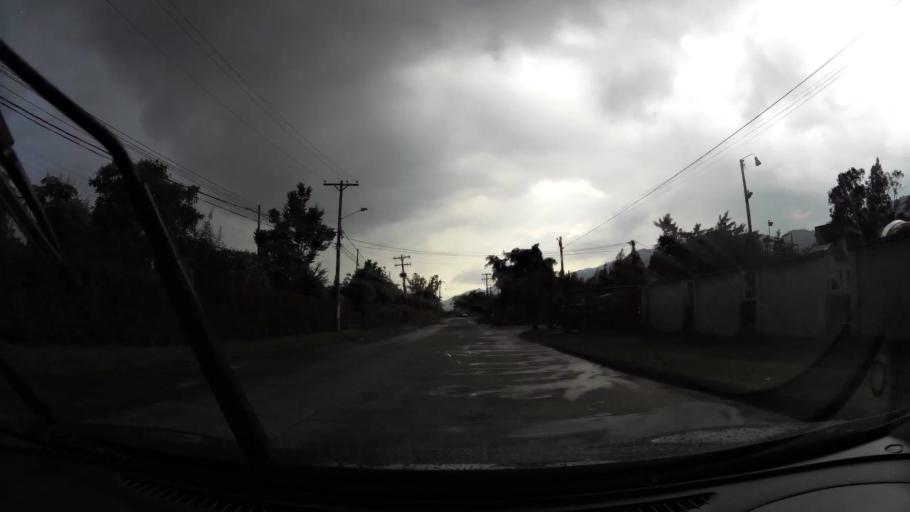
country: CO
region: Cundinamarca
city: Chia
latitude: 4.8539
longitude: -74.0666
